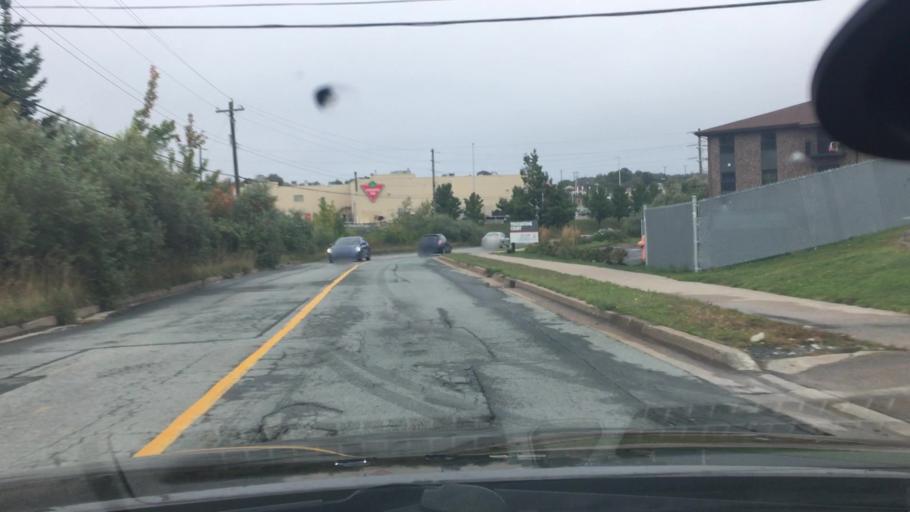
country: CA
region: Nova Scotia
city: Dartmouth
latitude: 44.7710
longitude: -63.6967
